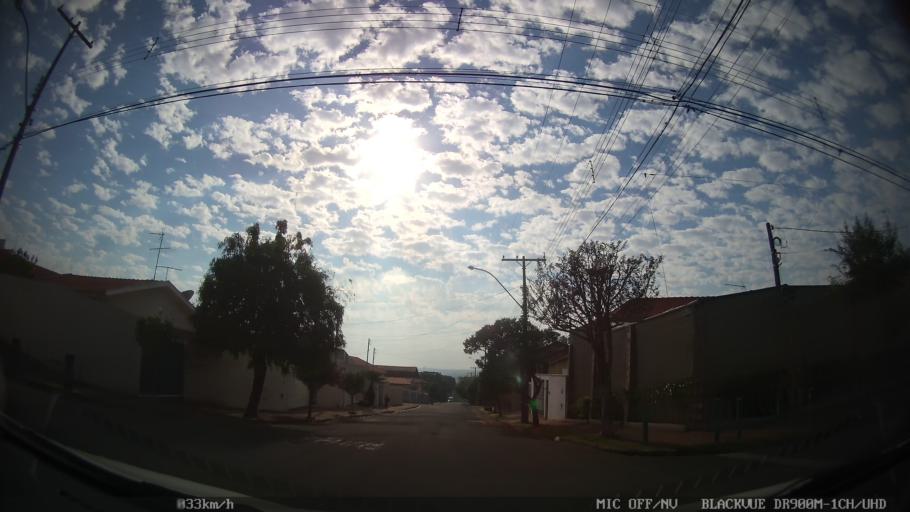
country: BR
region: Sao Paulo
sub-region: Americana
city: Americana
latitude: -22.7259
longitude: -47.3347
